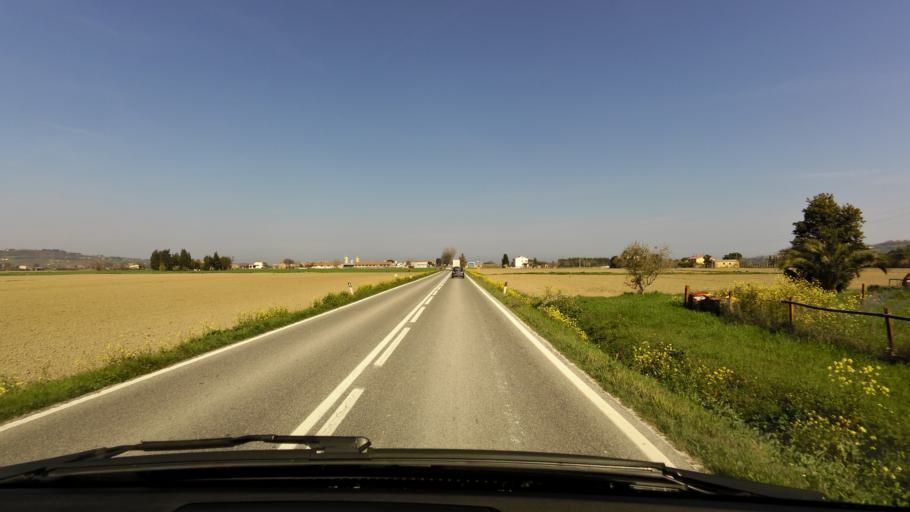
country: IT
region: The Marches
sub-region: Provincia di Macerata
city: Potenza Picena
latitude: 43.3877
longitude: 13.6267
